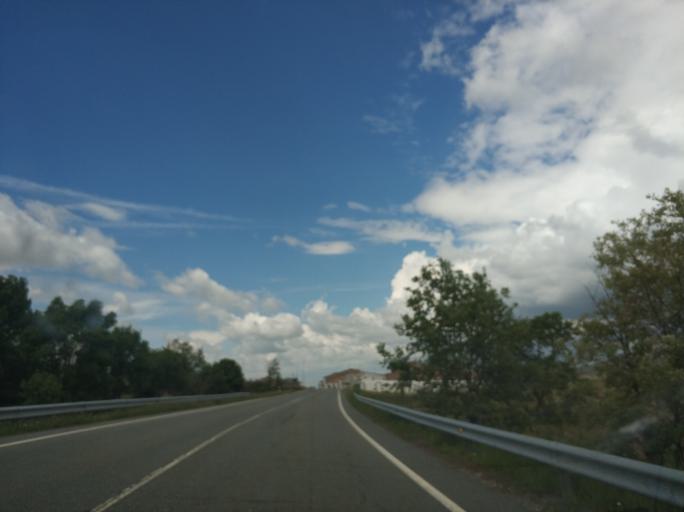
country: ES
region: Castille and Leon
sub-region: Provincia de Salamanca
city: Nava de Bejar
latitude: 40.4722
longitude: -5.6794
